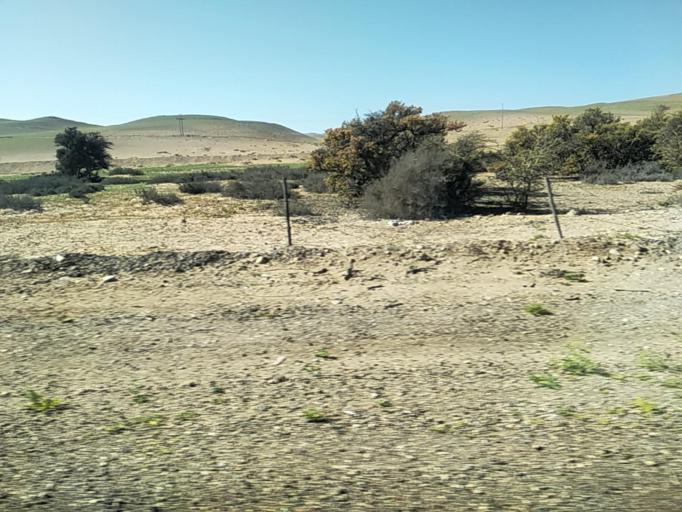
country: CL
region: Atacama
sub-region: Provincia de Copiapo
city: Copiapo
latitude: -27.3449
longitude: -70.7476
